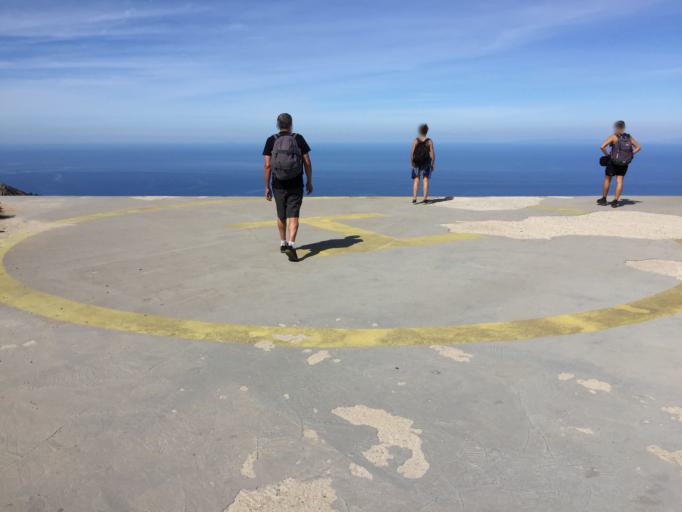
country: IT
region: Tuscany
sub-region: Provincia di Livorno
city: Marciana
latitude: 42.7715
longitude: 10.1683
